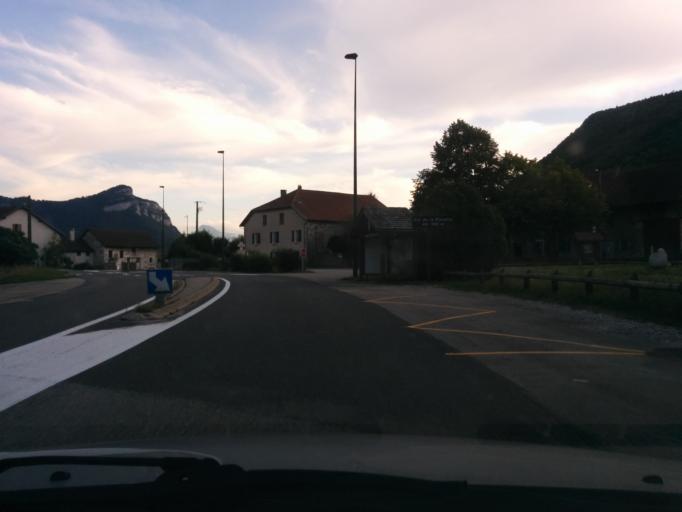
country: FR
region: Rhone-Alpes
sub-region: Departement de l'Isere
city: La Buisse
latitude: 45.3305
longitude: 5.6582
